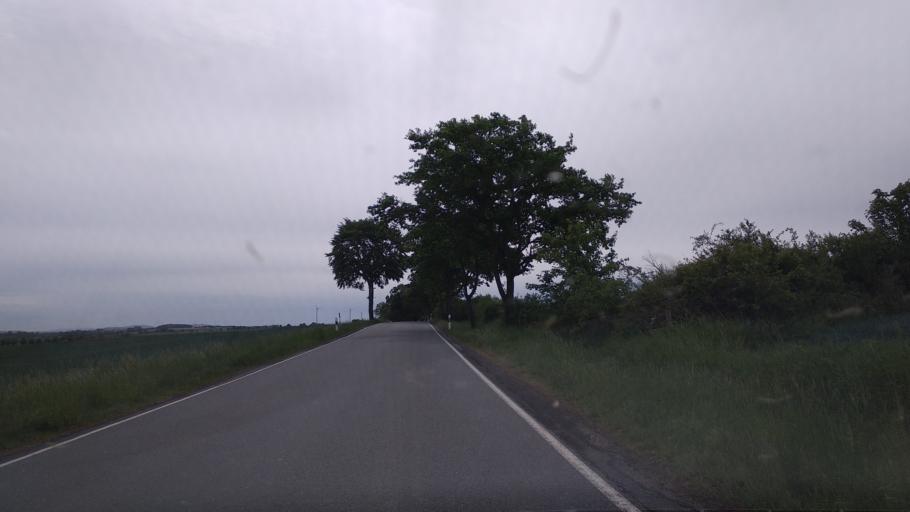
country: DE
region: North Rhine-Westphalia
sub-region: Regierungsbezirk Detmold
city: Willebadessen
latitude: 51.6100
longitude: 9.1121
